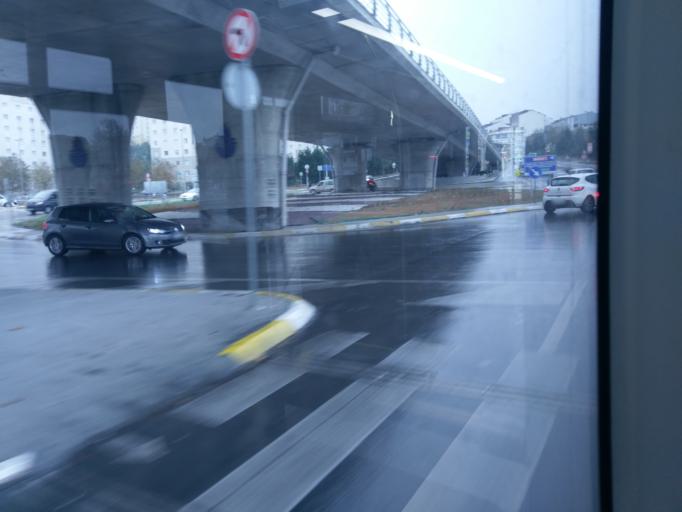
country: TR
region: Istanbul
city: Mahmutbey
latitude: 41.0338
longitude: 28.7687
